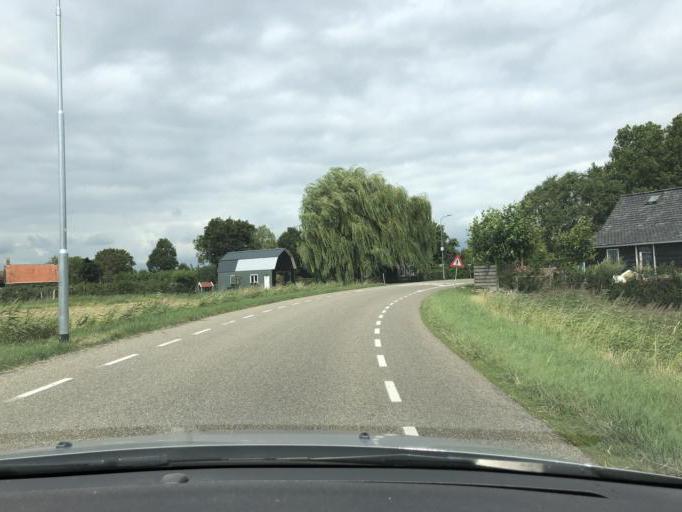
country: NL
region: Zeeland
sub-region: Gemeente Reimerswaal
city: Yerseke
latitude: 51.4249
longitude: 4.0720
